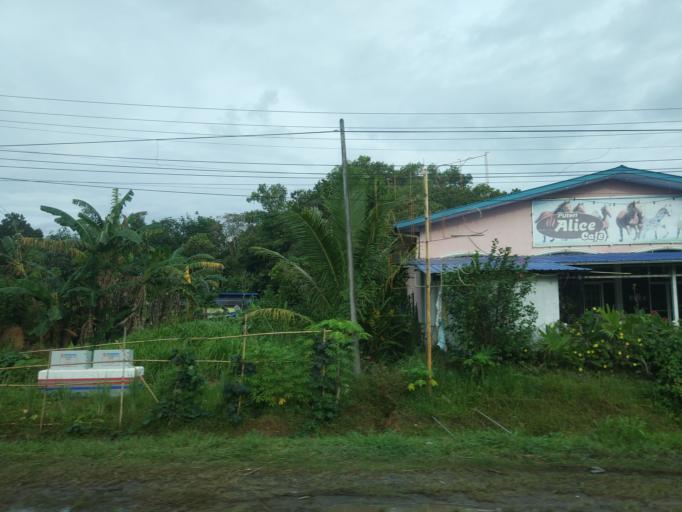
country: MY
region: Sabah
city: Kota Kinabalu
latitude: 6.1288
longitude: 116.2148
